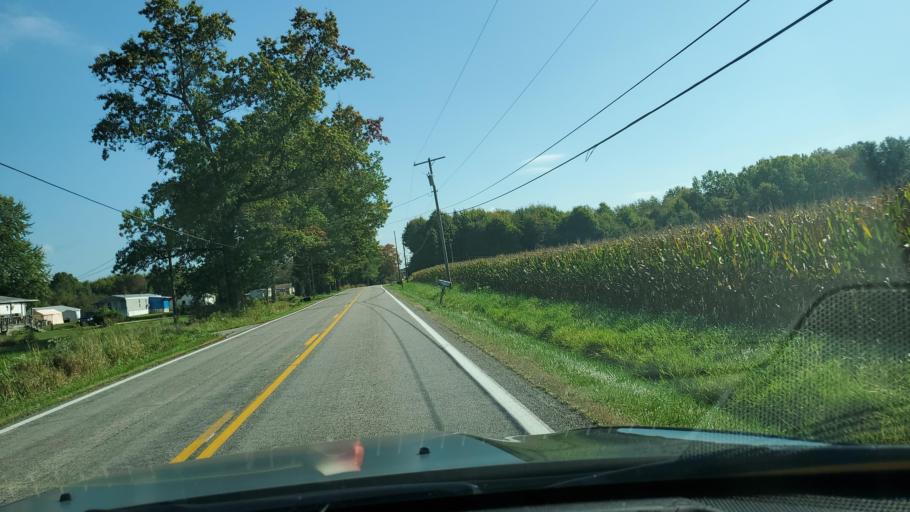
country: US
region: Ohio
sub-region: Trumbull County
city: Cortland
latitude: 41.3886
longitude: -80.6202
